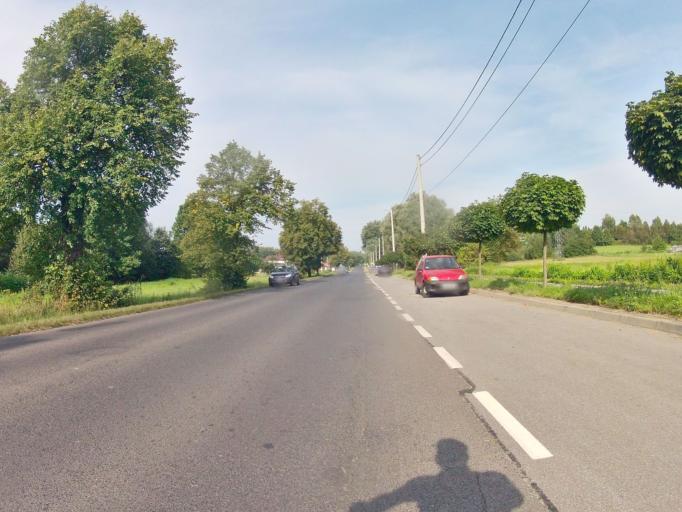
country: PL
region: Subcarpathian Voivodeship
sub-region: Powiat jasielski
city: Jaslo
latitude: 49.7533
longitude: 21.4518
